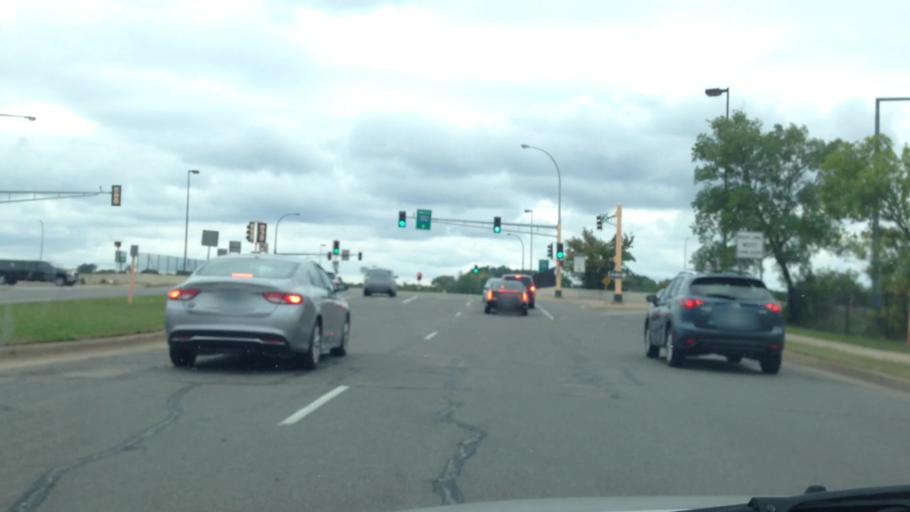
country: US
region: Minnesota
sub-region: Hennepin County
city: Saint Louis Park
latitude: 44.9703
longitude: -93.3706
